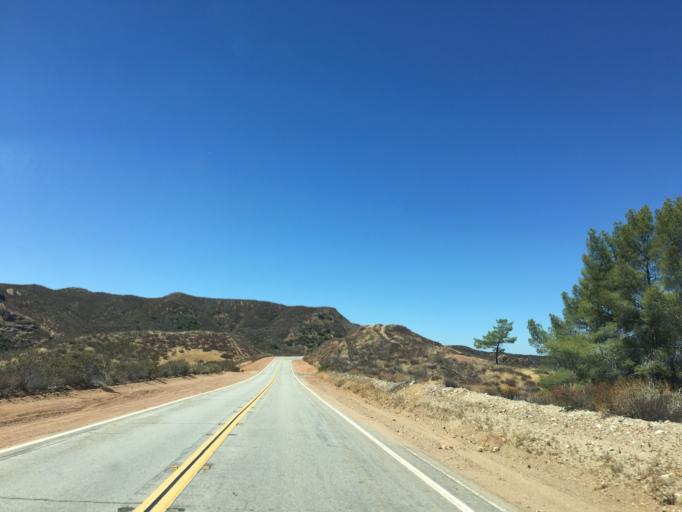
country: US
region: California
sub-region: Los Angeles County
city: Castaic
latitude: 34.5505
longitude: -118.5439
